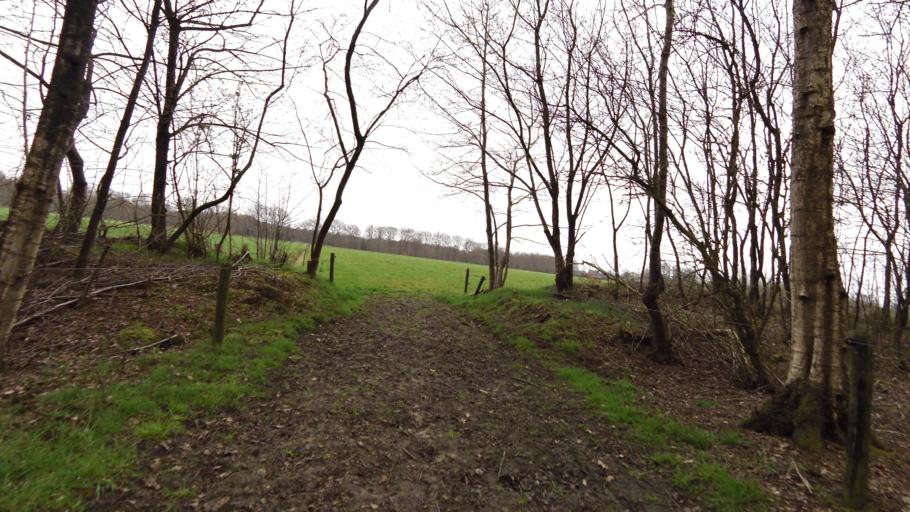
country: NL
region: Gelderland
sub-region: Gemeente Barneveld
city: Zwartebroek
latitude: 52.1938
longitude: 5.4944
